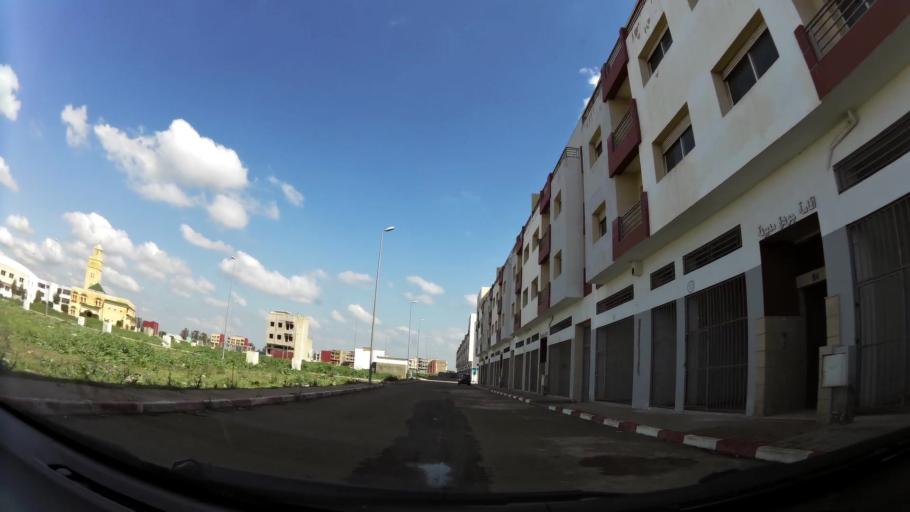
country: MA
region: Grand Casablanca
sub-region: Mediouna
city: Mediouna
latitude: 33.4495
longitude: -7.5069
